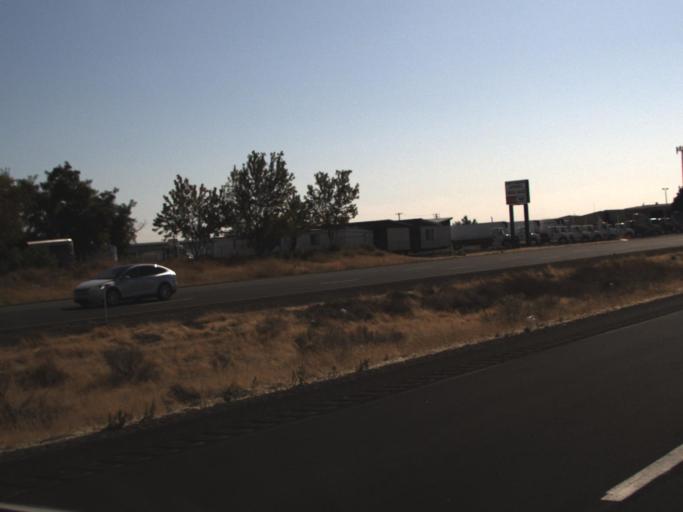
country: US
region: Washington
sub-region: Franklin County
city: Pasco
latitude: 46.2583
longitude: -119.0847
